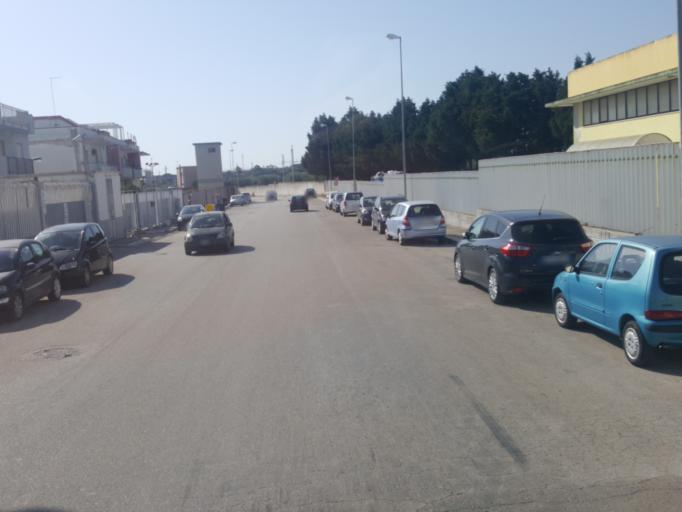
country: IT
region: Apulia
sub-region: Provincia di Barletta - Andria - Trani
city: Barletta
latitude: 41.3085
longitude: 16.3055
